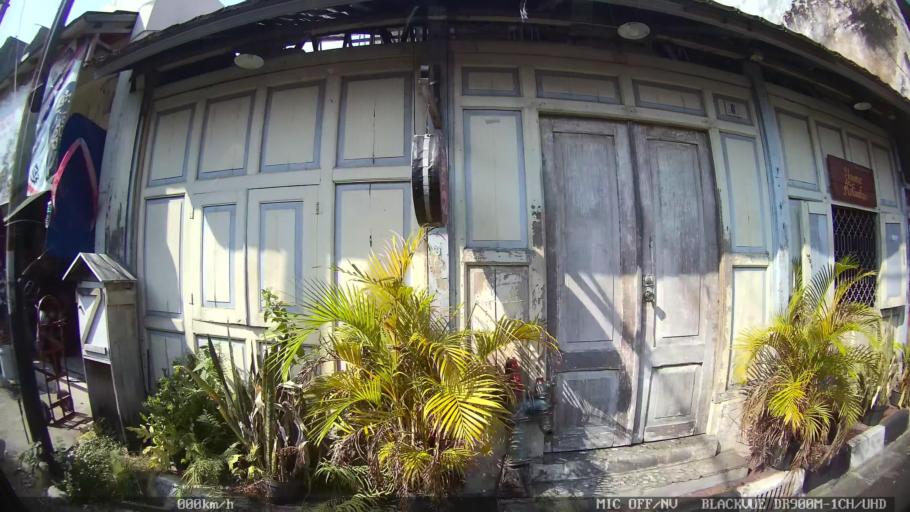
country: ID
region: Daerah Istimewa Yogyakarta
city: Yogyakarta
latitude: -7.7975
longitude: 110.3671
